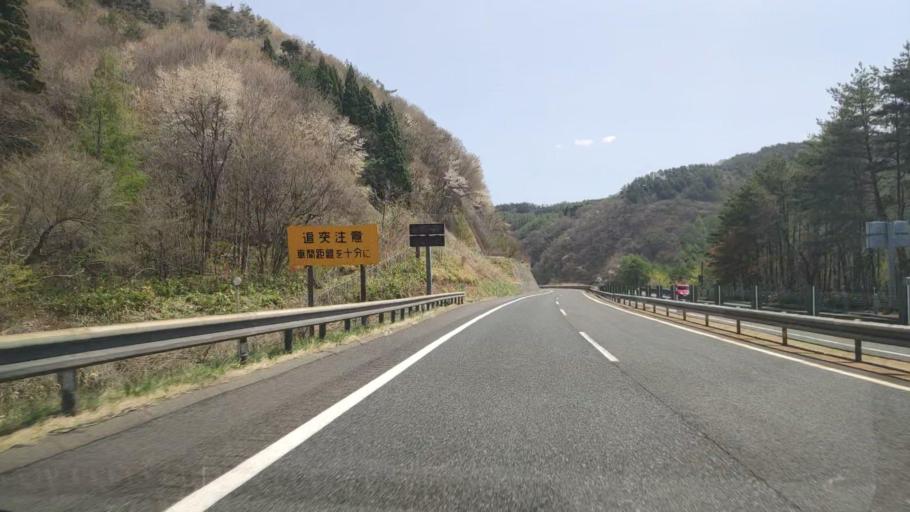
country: JP
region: Iwate
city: Ichinohe
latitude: 40.2228
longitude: 141.2546
